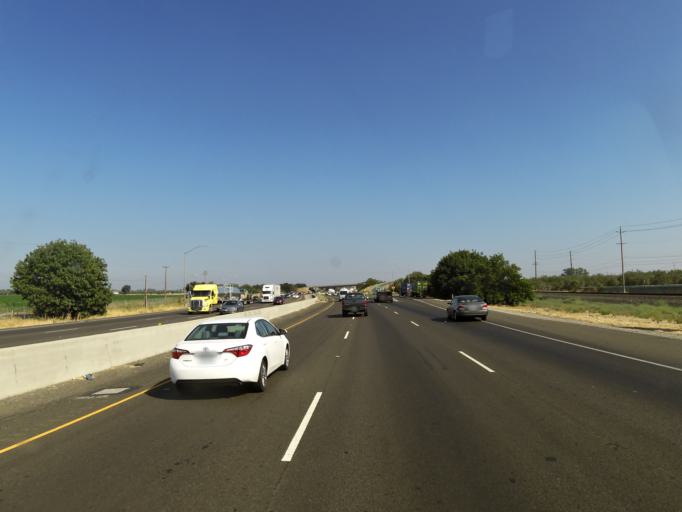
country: US
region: California
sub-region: San Joaquin County
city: Ripon
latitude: 37.7289
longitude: -121.1083
